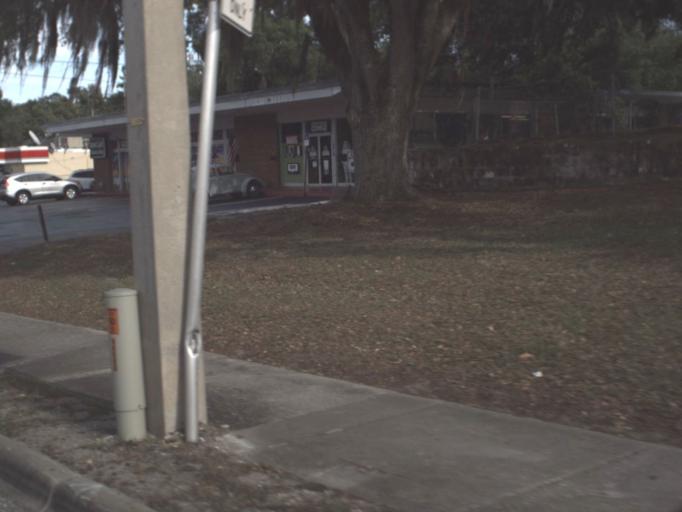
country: US
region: Florida
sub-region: Marion County
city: Ocala
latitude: 29.1869
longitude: -82.1235
